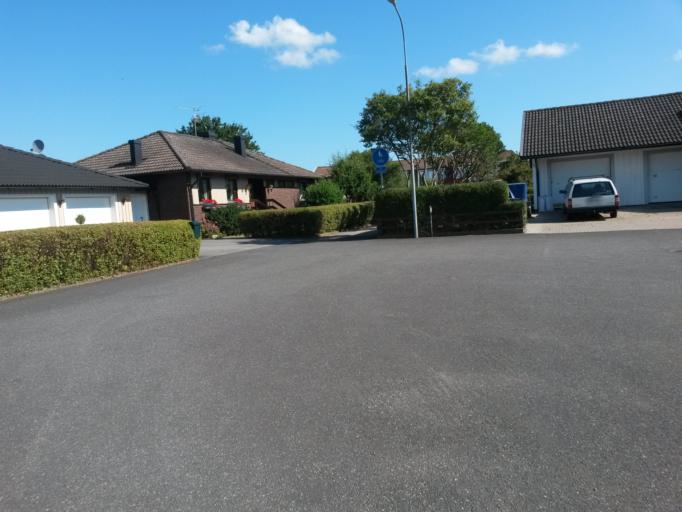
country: SE
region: Vaestra Goetaland
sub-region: Vargarda Kommun
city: Vargarda
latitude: 58.0399
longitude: 12.8145
